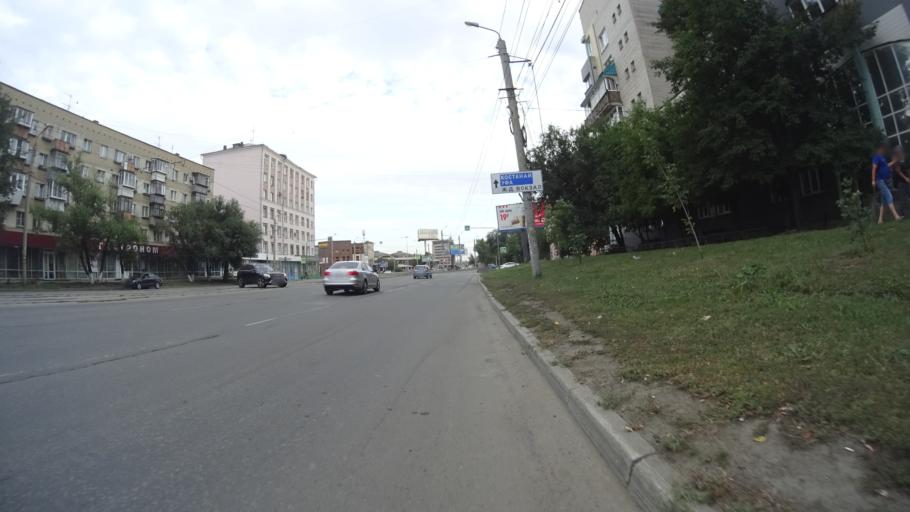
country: RU
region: Chelyabinsk
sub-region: Gorod Chelyabinsk
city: Chelyabinsk
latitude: 55.1447
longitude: 61.4132
